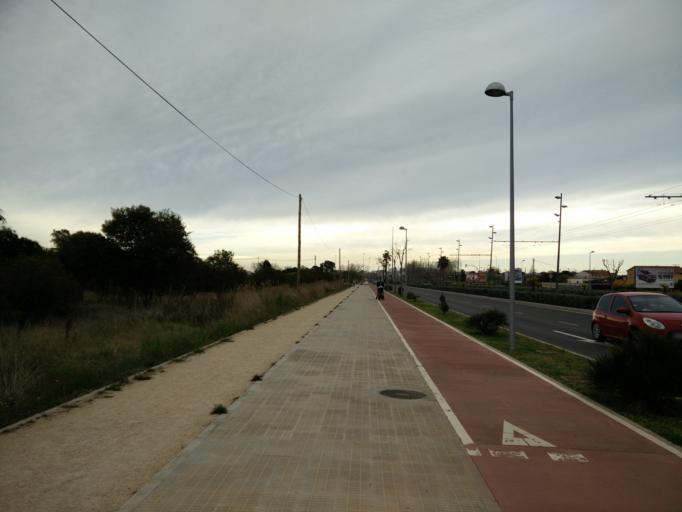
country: ES
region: Valencia
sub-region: Provincia de Castello
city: Castello de la Plana
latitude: 39.9803
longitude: -0.0067
